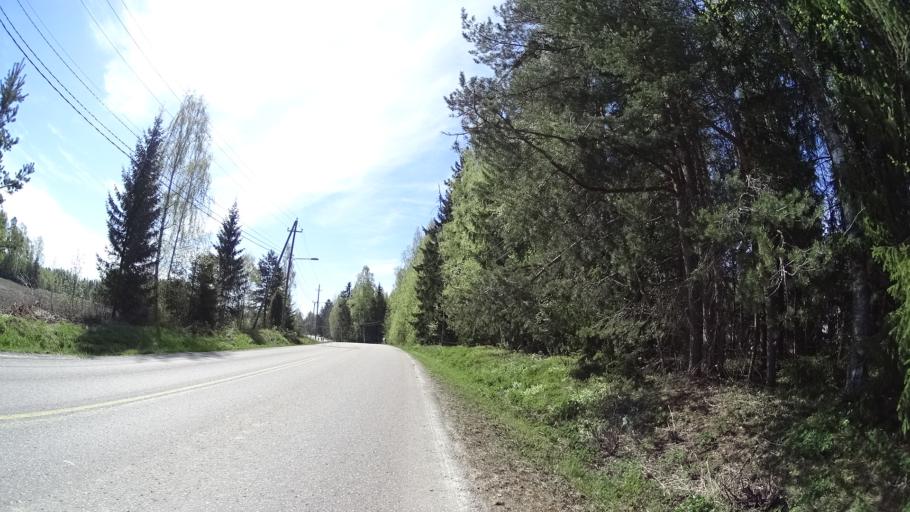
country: FI
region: Uusimaa
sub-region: Helsinki
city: Nurmijaervi
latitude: 60.3717
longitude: 24.8374
